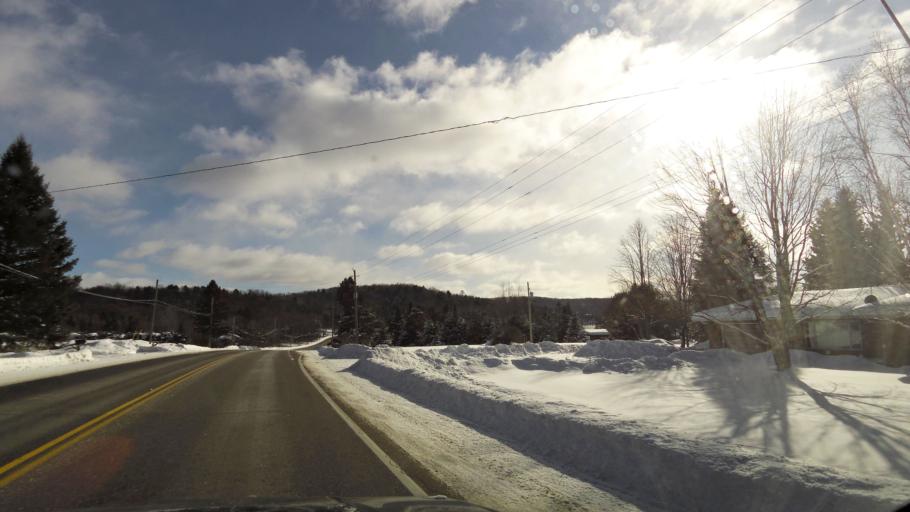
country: CA
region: Ontario
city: Bancroft
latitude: 45.0584
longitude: -78.5172
